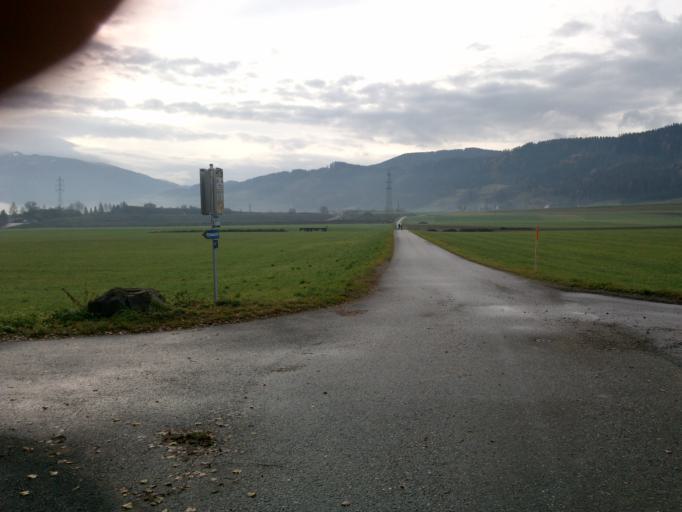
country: AT
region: Styria
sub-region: Politischer Bezirk Murtal
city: Fohnsdorf
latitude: 47.1733
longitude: 14.6975
